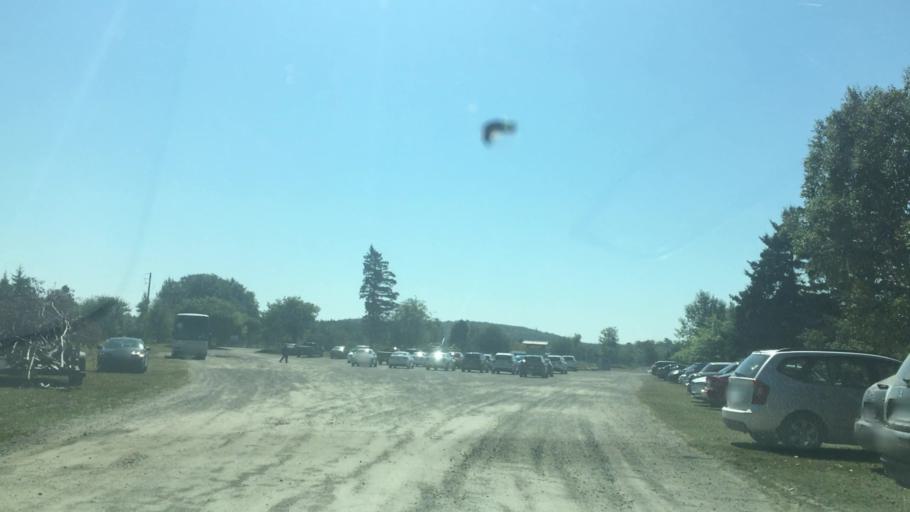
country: CA
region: Nova Scotia
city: Antigonish
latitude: 45.1388
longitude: -61.9830
